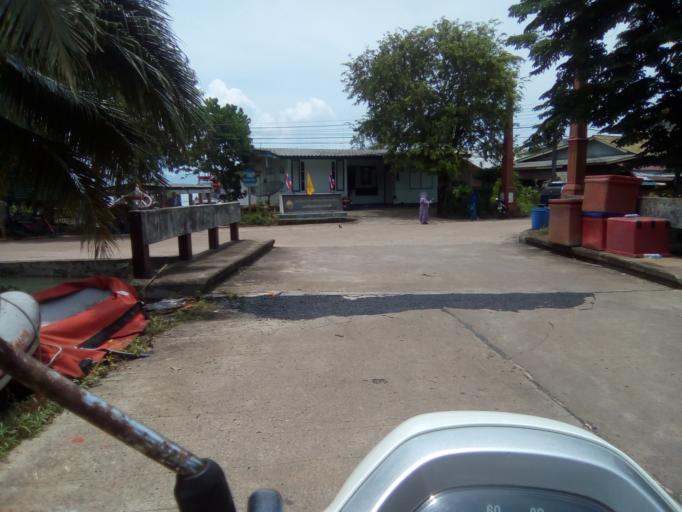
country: TH
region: Krabi
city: Ko Lanta
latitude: 7.5330
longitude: 99.0918
